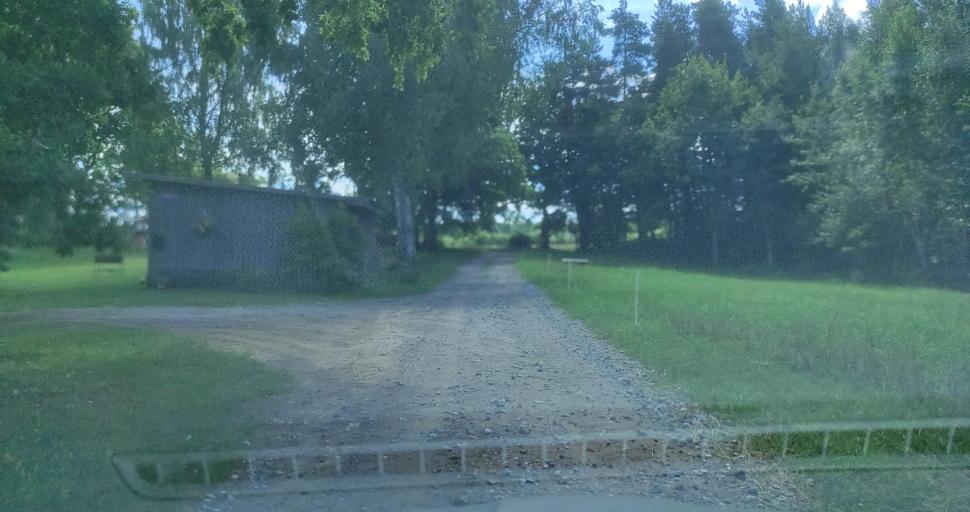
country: LV
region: Alsunga
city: Alsunga
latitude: 57.0252
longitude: 21.7040
